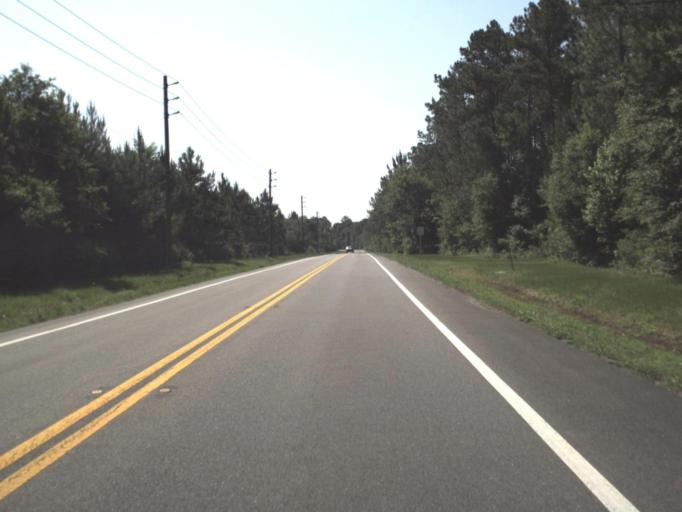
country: US
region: Florida
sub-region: Nassau County
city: Nassau Village-Ratliff
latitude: 30.4933
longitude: -81.7388
